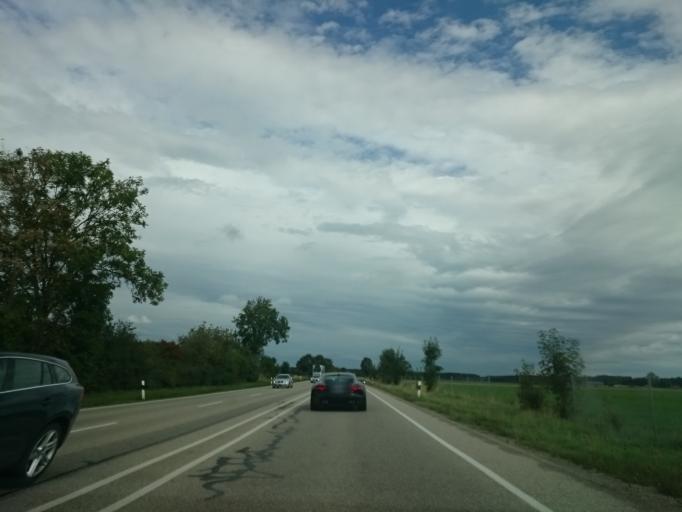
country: DE
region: Bavaria
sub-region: Swabia
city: Rieden
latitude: 47.9629
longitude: 10.6843
